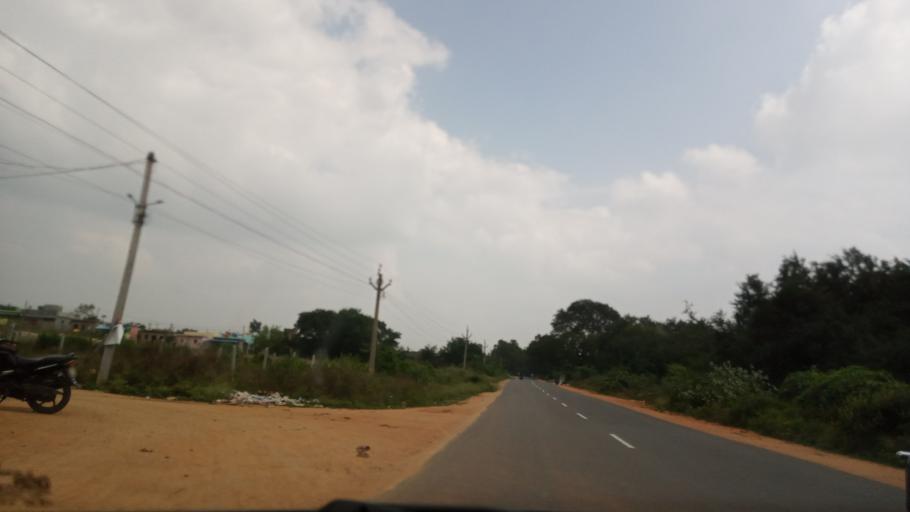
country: IN
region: Andhra Pradesh
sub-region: Chittoor
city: Madanapalle
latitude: 13.6368
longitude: 78.6383
